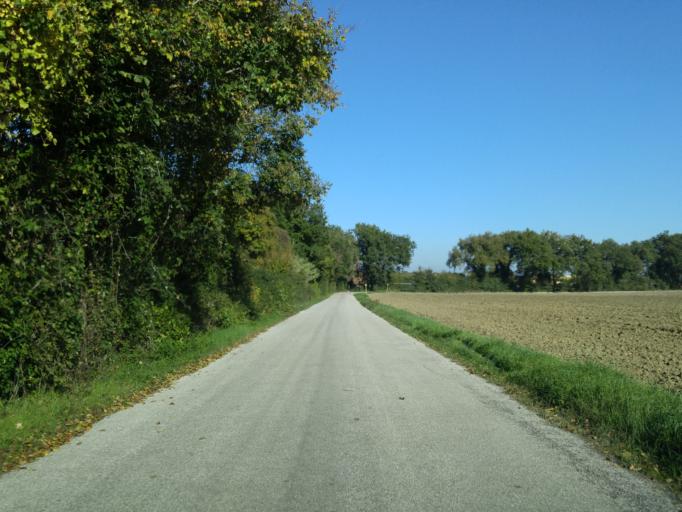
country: IT
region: The Marches
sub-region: Provincia di Pesaro e Urbino
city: Tavernelle
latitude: 43.7218
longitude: 12.8892
